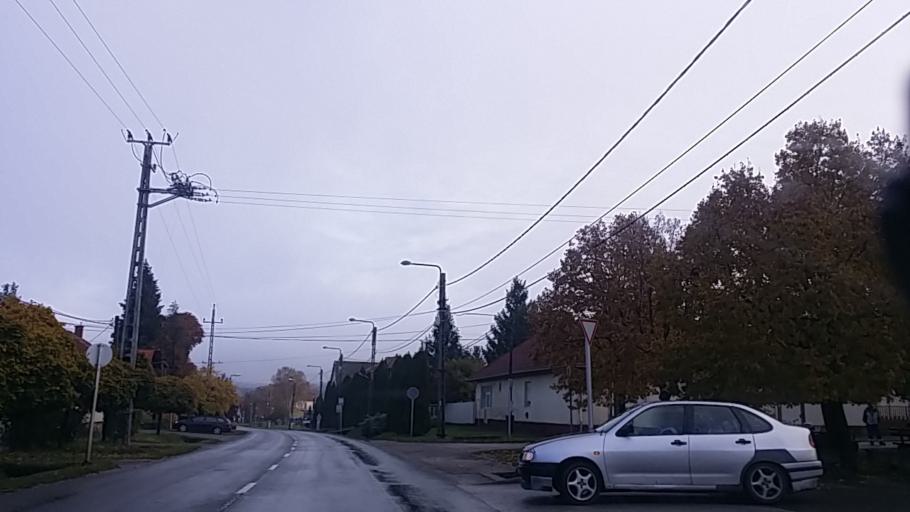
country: HU
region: Heves
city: Belapatfalva
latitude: 48.0556
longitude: 20.3510
